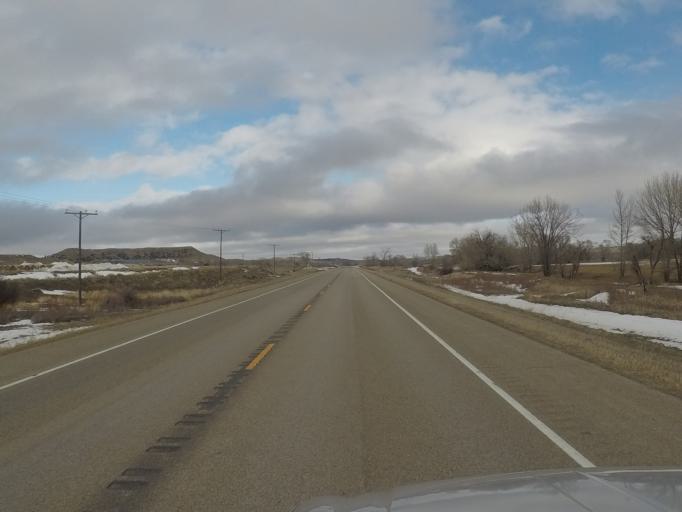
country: US
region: Montana
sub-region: Golden Valley County
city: Ryegate
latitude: 46.3176
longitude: -109.4093
